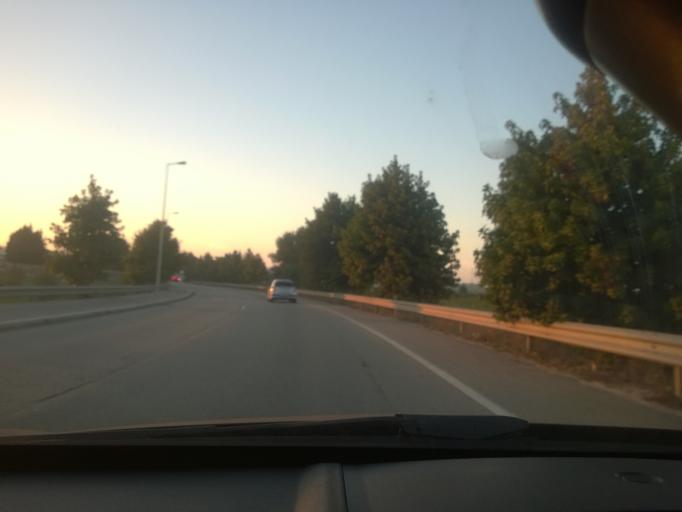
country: PT
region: Porto
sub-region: Matosinhos
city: Santa Cruz do Bispo
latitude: 41.2261
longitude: -8.6963
